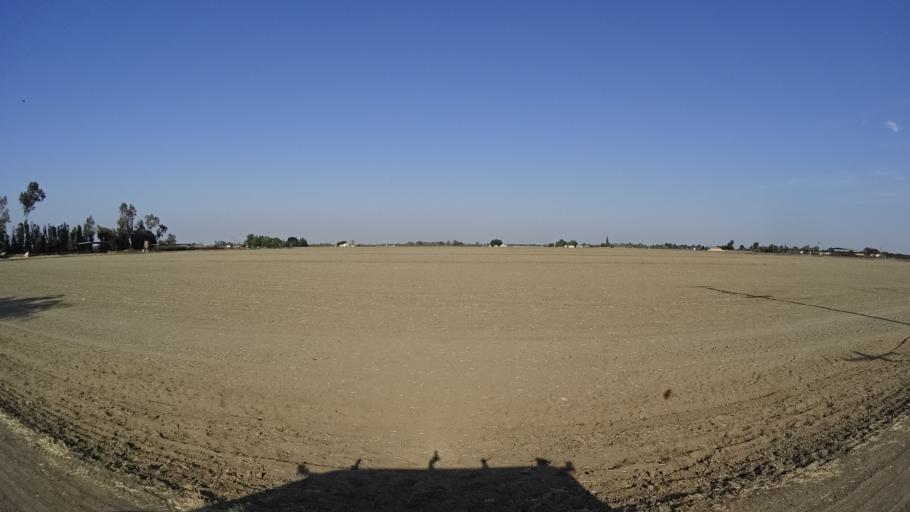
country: US
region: California
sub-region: Fresno County
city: Riverdale
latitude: 36.3761
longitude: -119.8431
